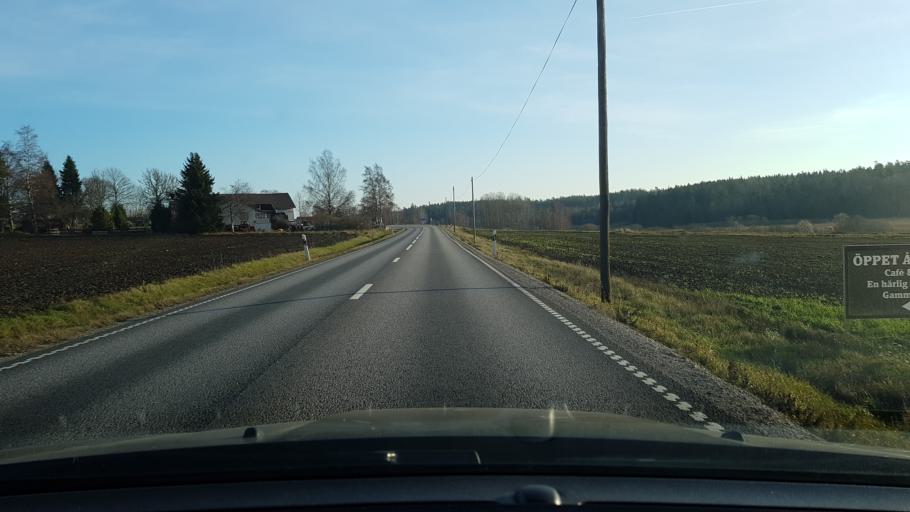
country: SE
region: Stockholm
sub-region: Norrtalje Kommun
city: Nykvarn
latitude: 59.7364
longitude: 18.2467
